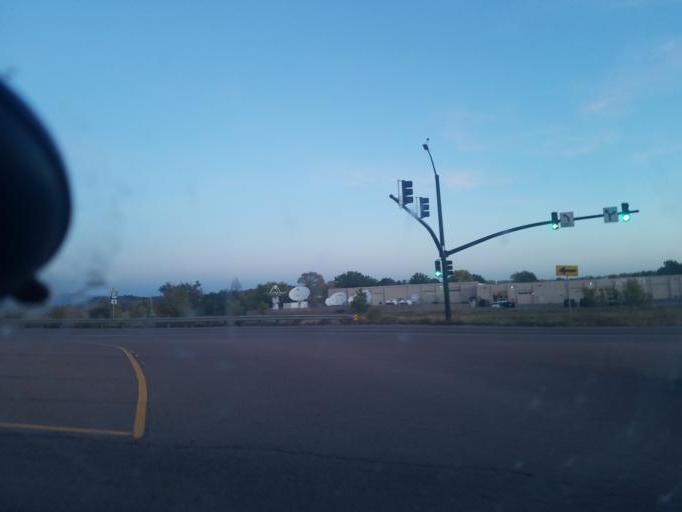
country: US
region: Colorado
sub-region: El Paso County
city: Cimarron Hills
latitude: 38.8389
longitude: -104.7185
